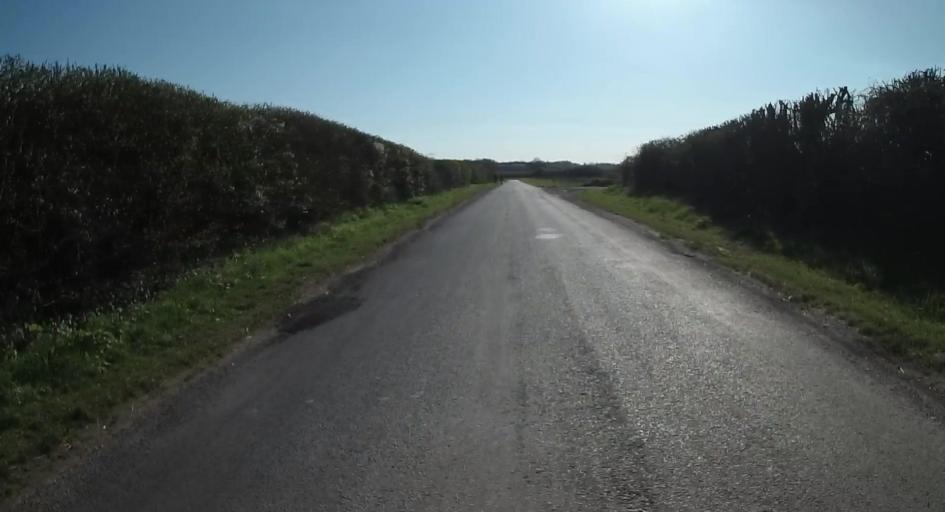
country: GB
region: England
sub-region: Hampshire
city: Basingstoke
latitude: 51.2792
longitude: -1.1309
